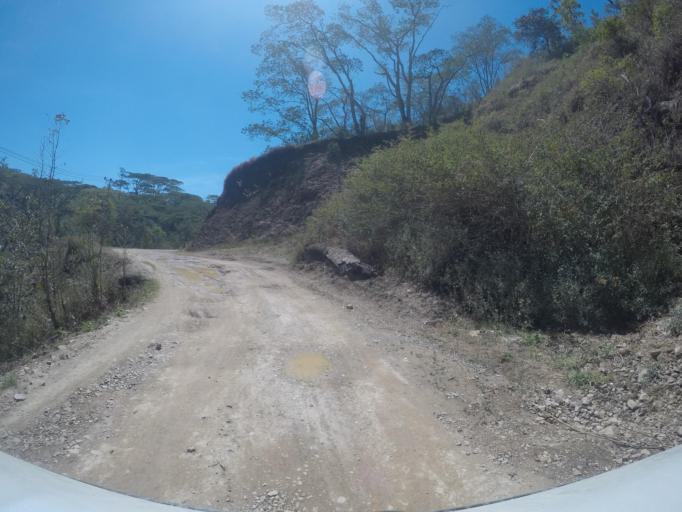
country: TL
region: Ermera
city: Gleno
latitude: -8.7902
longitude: 125.3749
